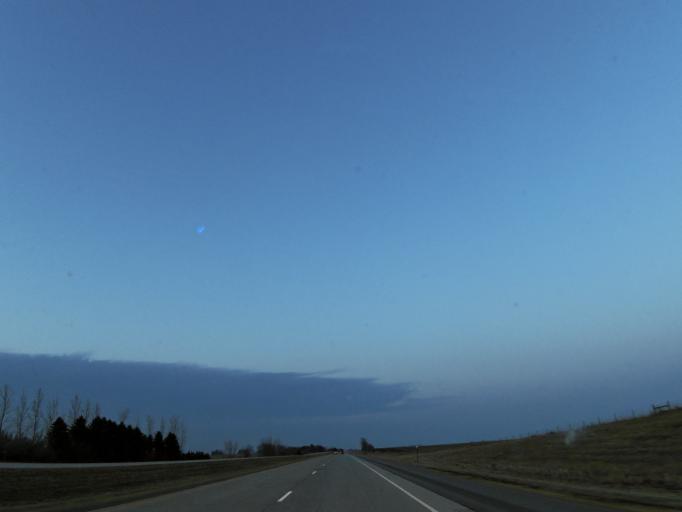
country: US
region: Minnesota
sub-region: Mower County
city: Grand Meadow
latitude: 43.7778
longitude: -92.6225
